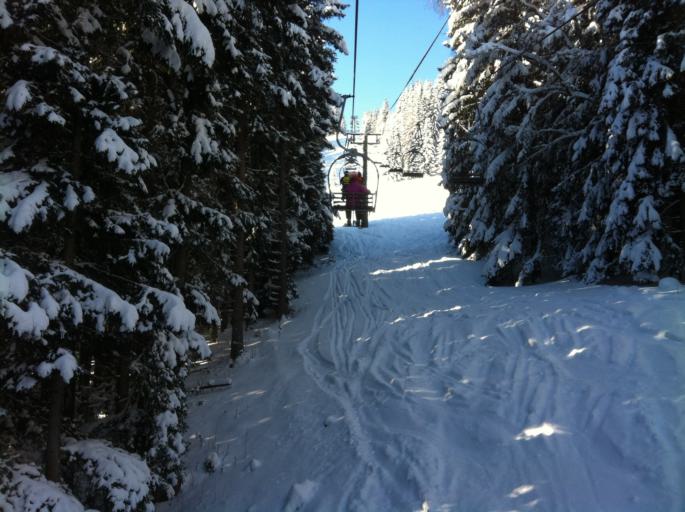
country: FR
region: Rhone-Alpes
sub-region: Departement de la Haute-Savoie
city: Saint-Gervais-les-Bains
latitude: 45.8557
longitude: 6.7098
